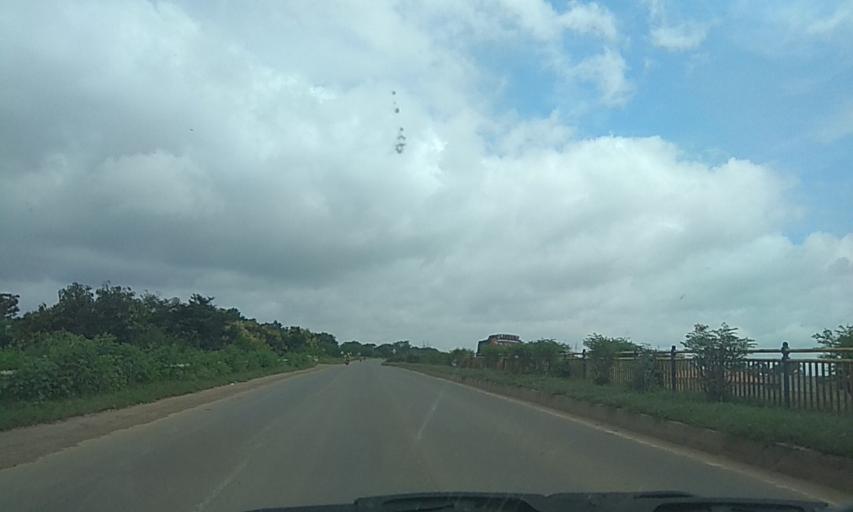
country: IN
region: Karnataka
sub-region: Dharwad
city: Kundgol
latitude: 15.2240
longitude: 75.1408
